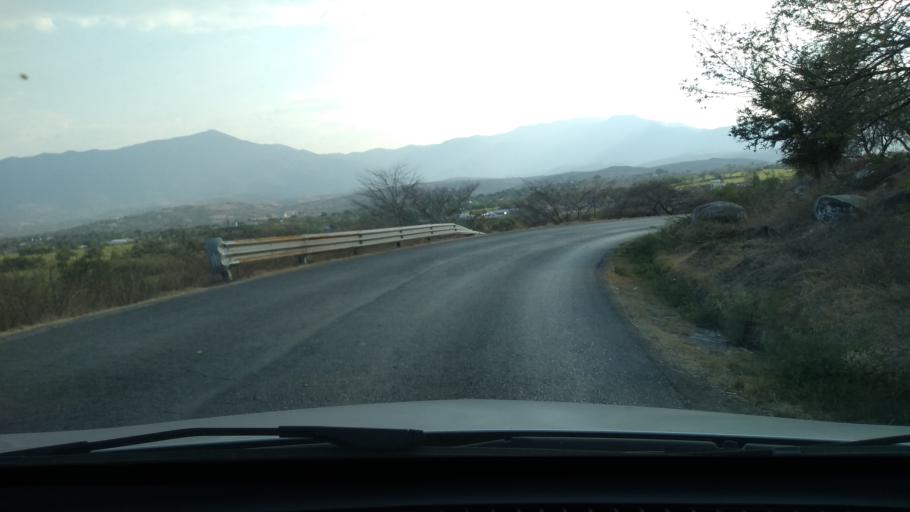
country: MX
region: Morelos
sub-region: Jojutla
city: Tehuixtla
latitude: 18.5720
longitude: -99.2642
